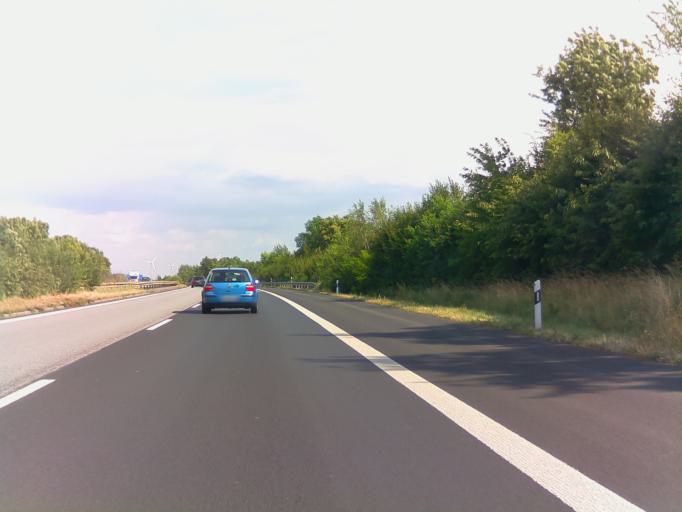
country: DE
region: Bavaria
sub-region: Regierungsbezirk Unterfranken
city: Rottendorf
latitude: 49.7942
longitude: 10.0575
